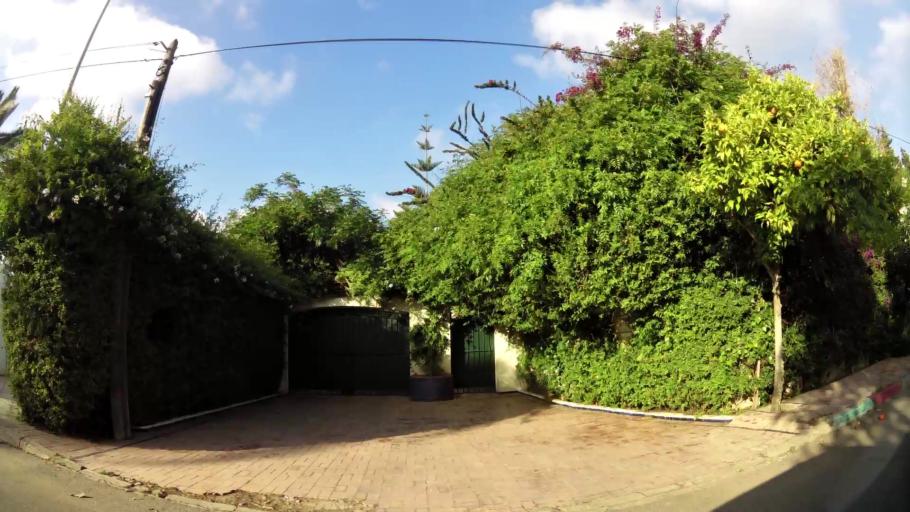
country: MA
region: Rabat-Sale-Zemmour-Zaer
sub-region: Rabat
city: Rabat
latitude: 33.9624
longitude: -6.8454
